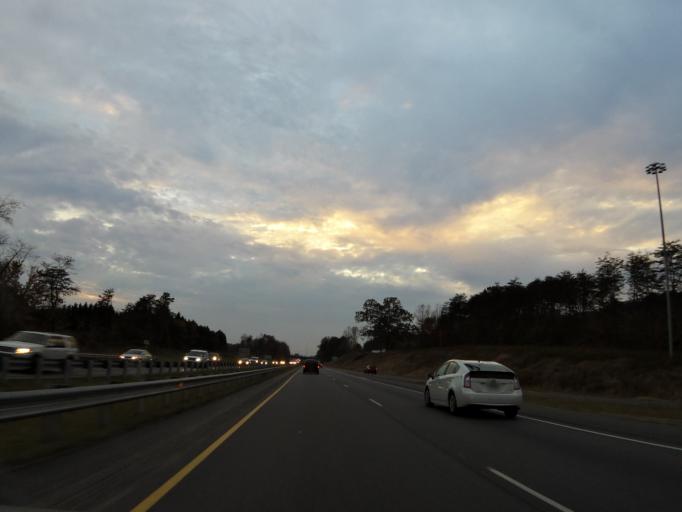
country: US
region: North Carolina
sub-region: Burke County
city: Morganton
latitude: 35.7218
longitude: -81.6589
